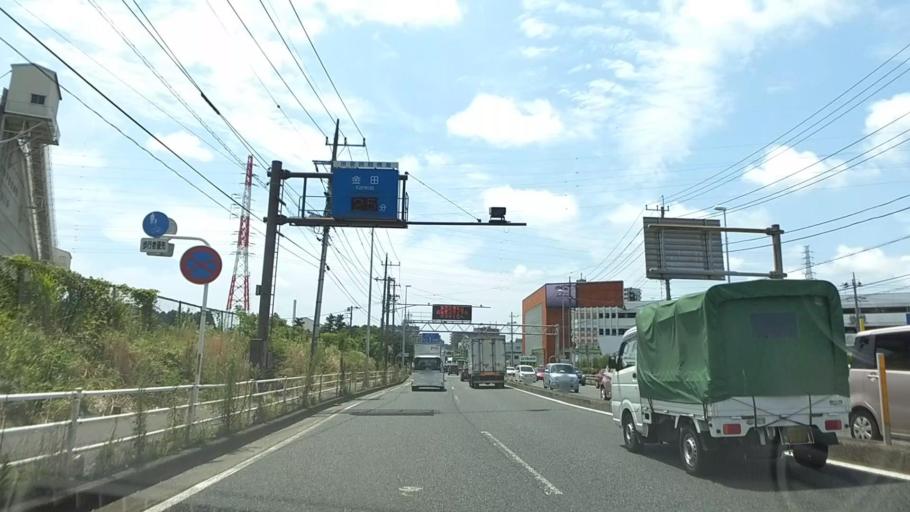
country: JP
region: Kanagawa
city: Minami-rinkan
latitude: 35.4969
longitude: 139.4661
